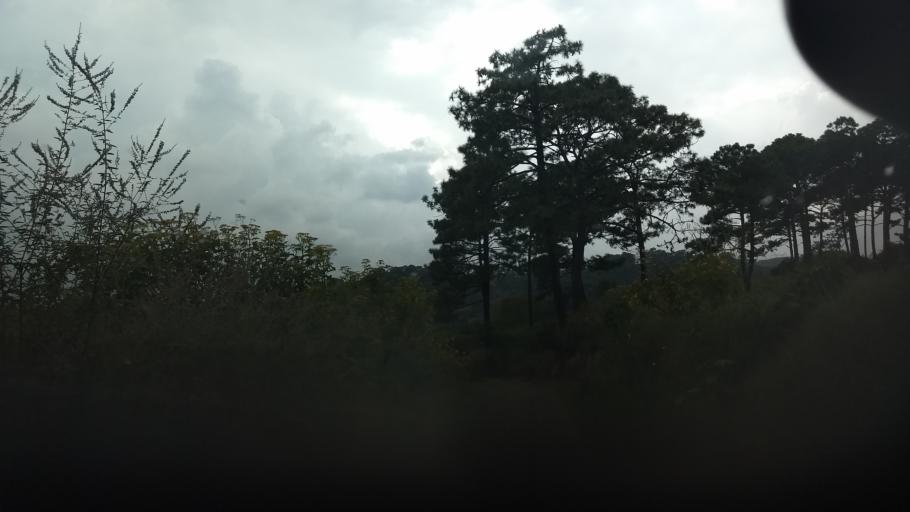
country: MX
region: Colima
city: Cofradia
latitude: 19.4679
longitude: -103.5366
